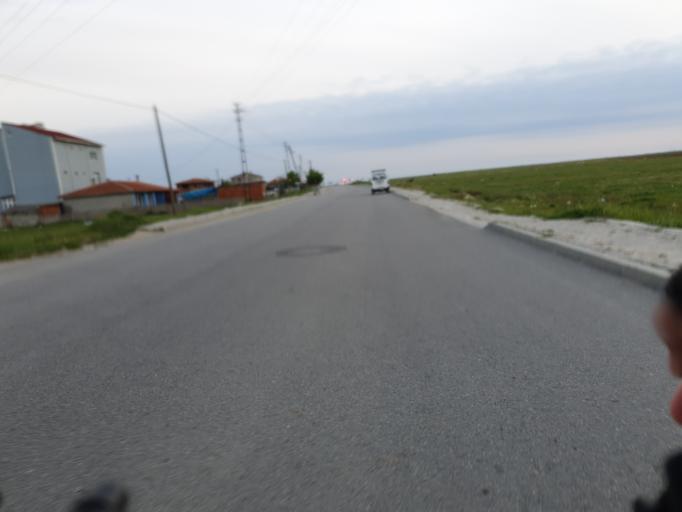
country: TR
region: Tekirdag
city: Saray
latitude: 41.4341
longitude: 27.9125
